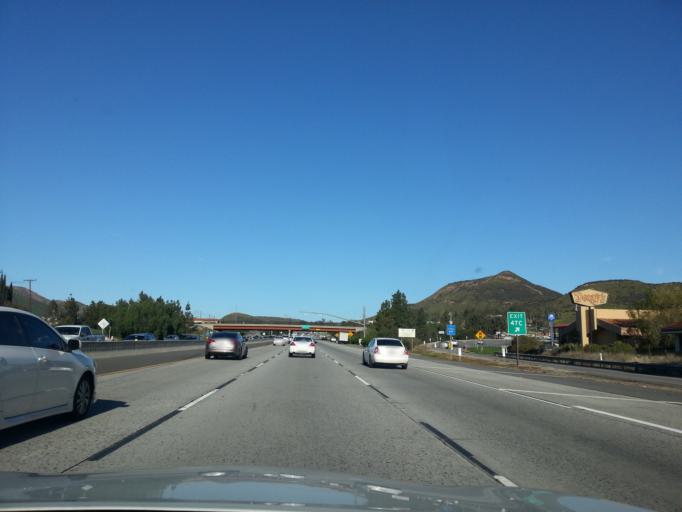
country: US
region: California
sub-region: Ventura County
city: Casa Conejo
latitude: 34.1884
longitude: -118.9358
